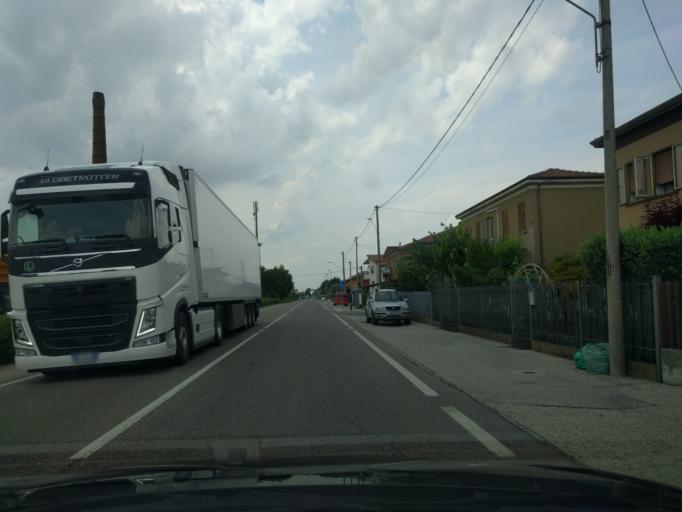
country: IT
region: Veneto
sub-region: Provincia di Rovigo
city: Lendinara
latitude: 45.0883
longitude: 11.5948
